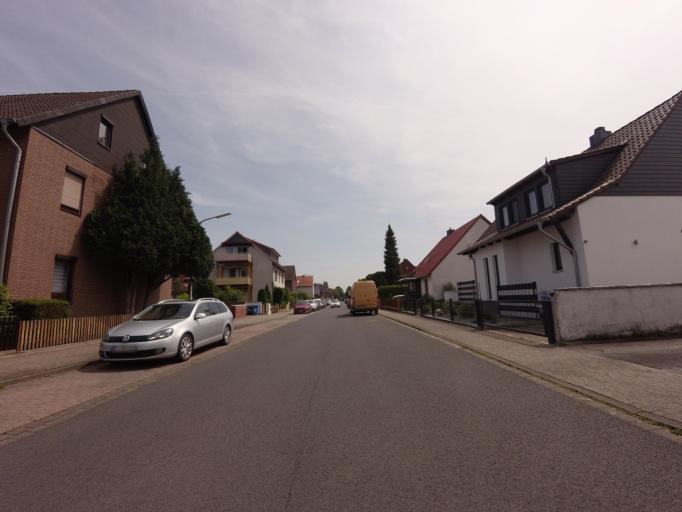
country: DE
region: Lower Saxony
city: Braunschweig
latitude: 52.3081
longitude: 10.4865
